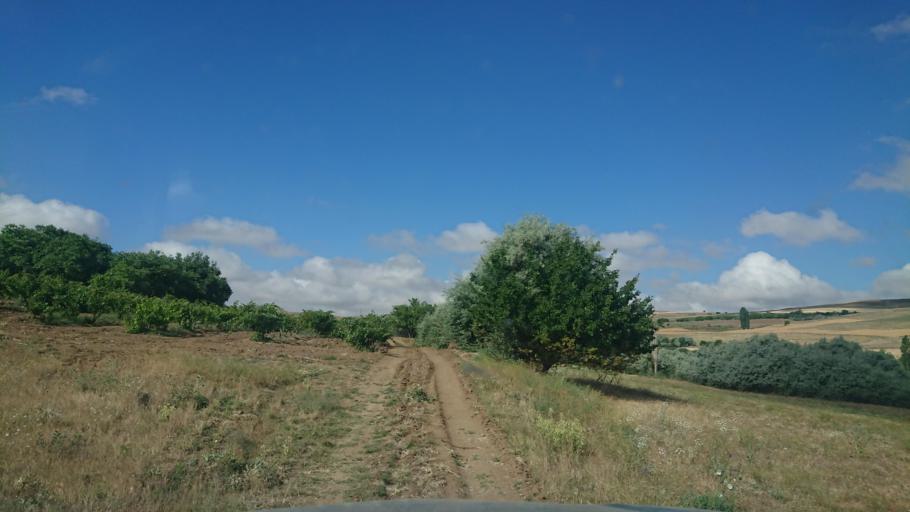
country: TR
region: Aksaray
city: Agacoren
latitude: 38.8510
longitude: 33.9343
